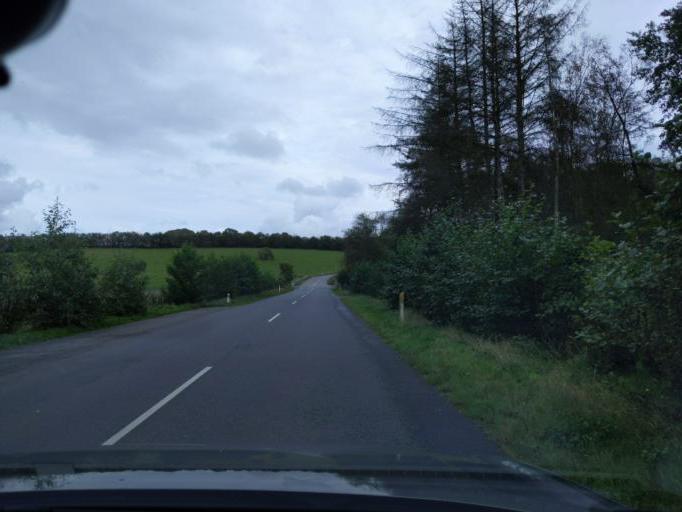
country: DK
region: Central Jutland
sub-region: Viborg Kommune
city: Viborg
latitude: 56.4168
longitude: 9.4594
